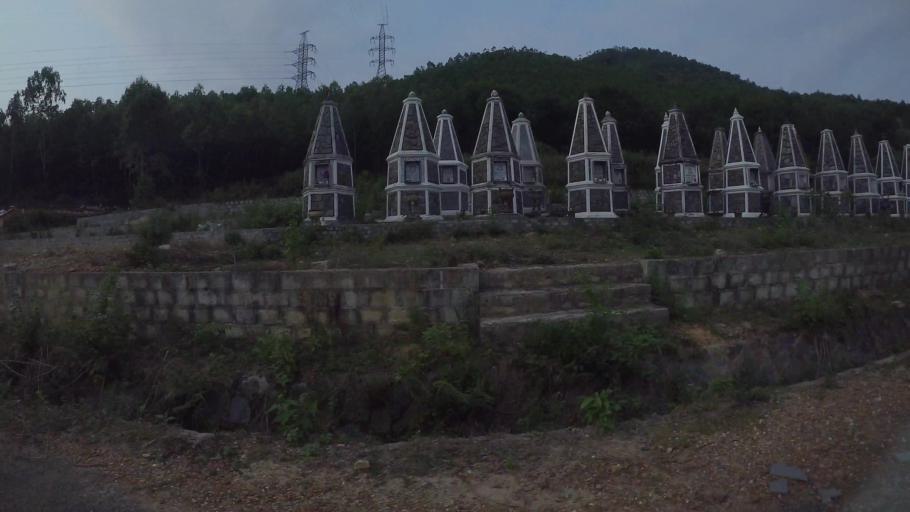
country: VN
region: Da Nang
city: Lien Chieu
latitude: 16.0632
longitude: 108.1106
